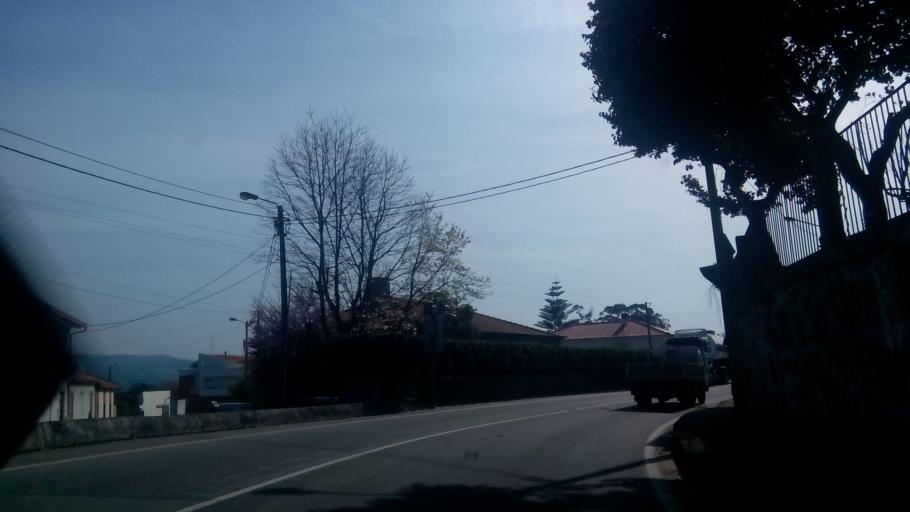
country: PT
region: Viana do Castelo
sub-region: Viana do Castelo
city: Darque
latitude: 41.6822
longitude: -8.7860
